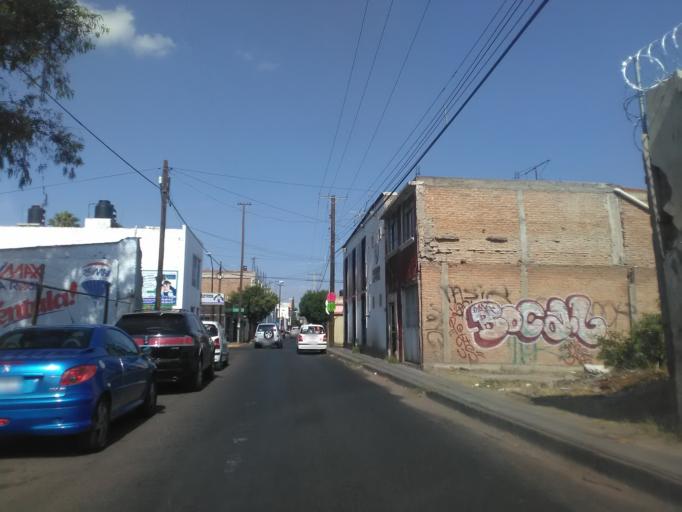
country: MX
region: Durango
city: Victoria de Durango
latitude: 24.0283
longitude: -104.6612
